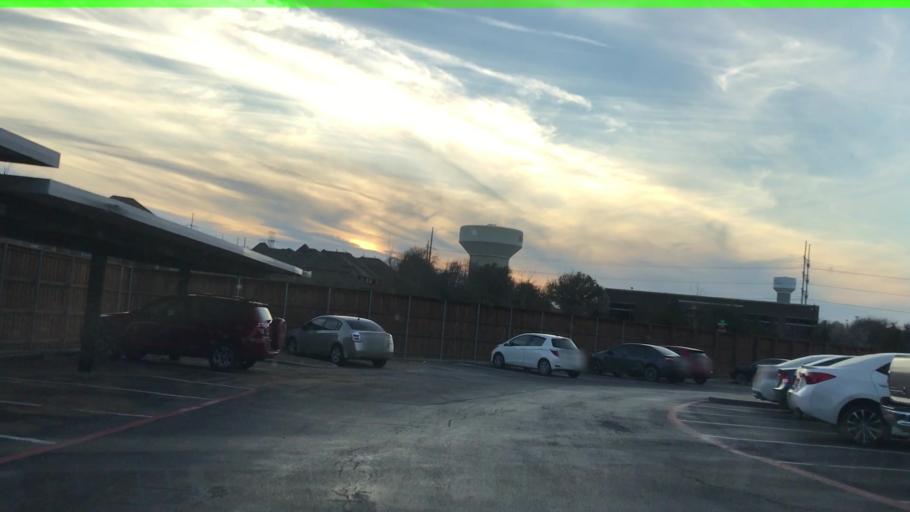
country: US
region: Texas
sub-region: Dallas County
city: Coppell
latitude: 32.9093
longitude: -96.9869
